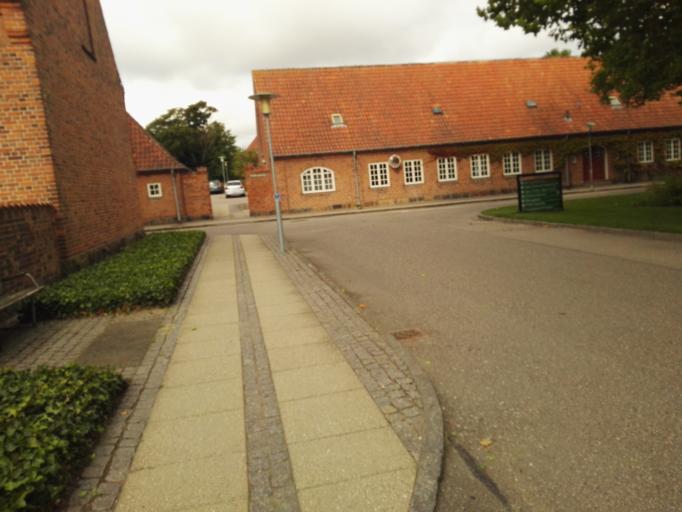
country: DK
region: Zealand
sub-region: Odsherred Kommune
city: Nykobing Sjaelland
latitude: 55.9088
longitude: 11.6596
